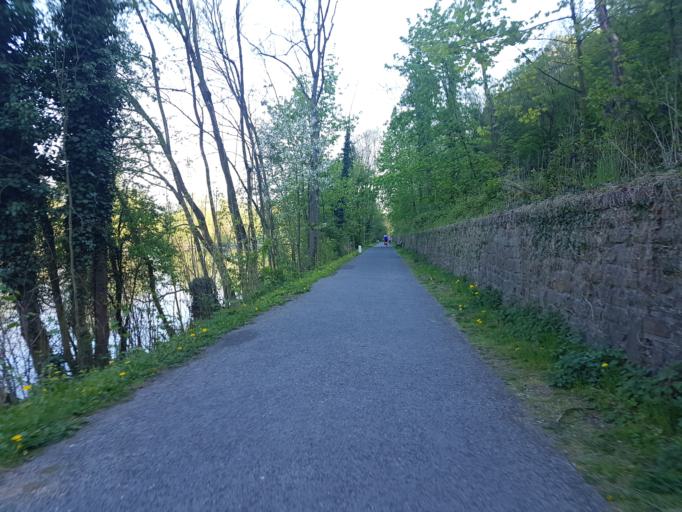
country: DE
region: North Rhine-Westphalia
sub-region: Regierungsbezirk Dusseldorf
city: Essen
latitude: 51.4341
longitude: 7.0857
